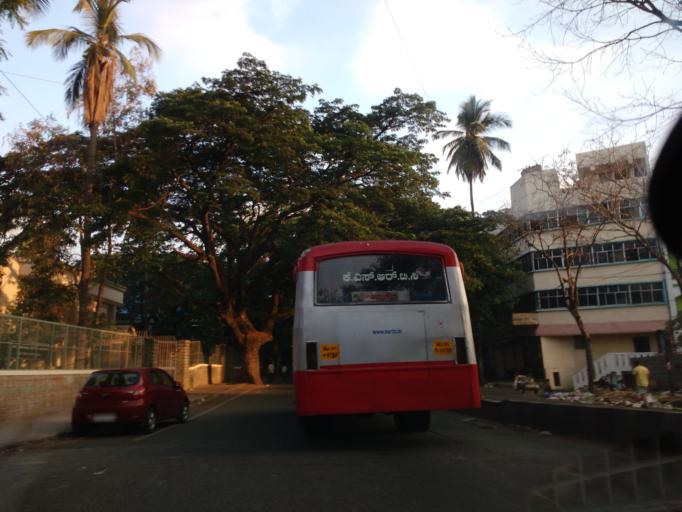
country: IN
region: Karnataka
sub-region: Bangalore Urban
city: Bangalore
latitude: 12.9943
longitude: 77.5555
